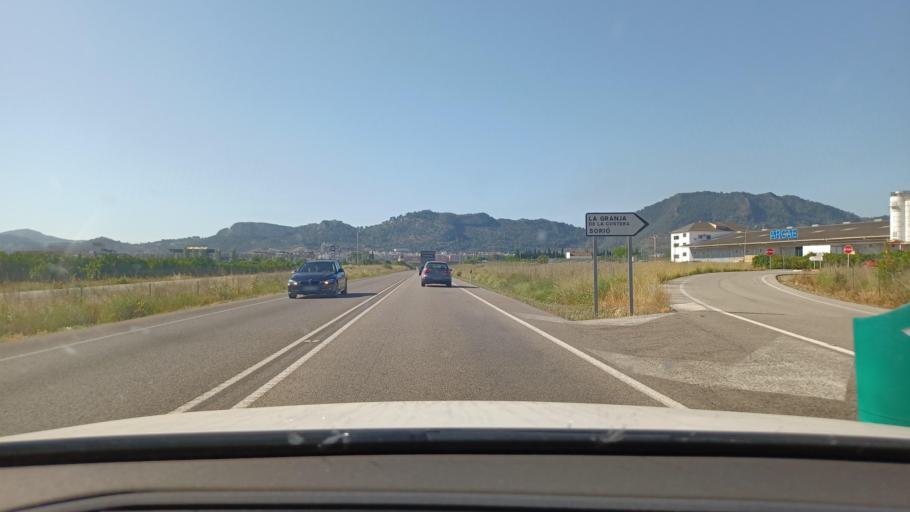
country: ES
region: Valencia
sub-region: Provincia de Valencia
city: Llosa de Ranes
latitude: 39.0082
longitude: -0.5321
